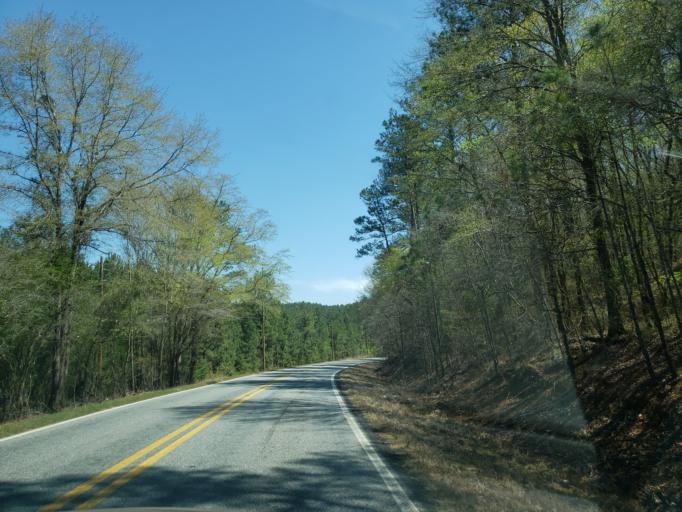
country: US
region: Alabama
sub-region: Elmore County
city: Tallassee
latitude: 32.6780
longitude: -85.8791
